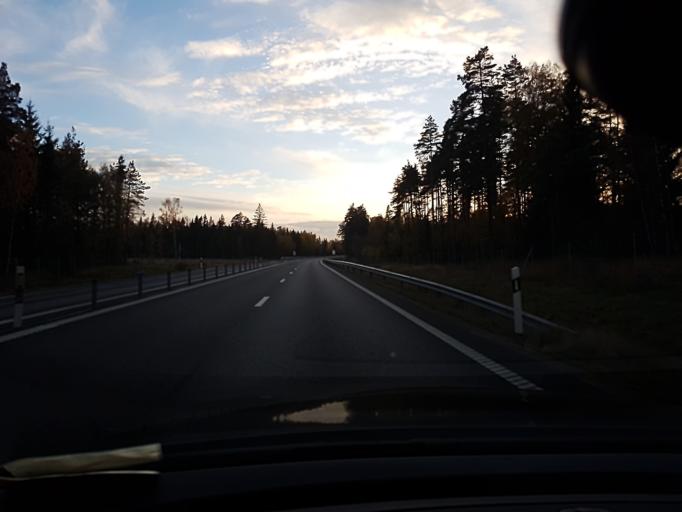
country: SE
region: Kronoberg
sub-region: Ljungby Kommun
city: Ljungby
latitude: 56.7948
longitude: 13.8516
